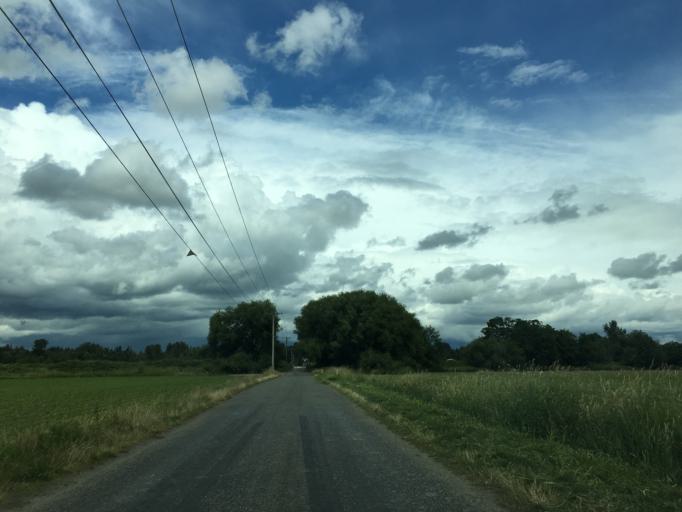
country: US
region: Washington
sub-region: Whatcom County
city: Lynden
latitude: 48.9245
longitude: -122.4964
